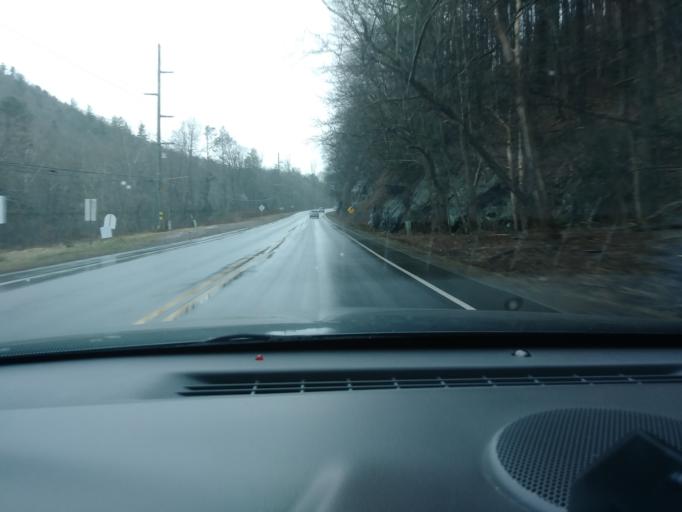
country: US
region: North Carolina
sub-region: Watauga County
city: Foscoe
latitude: 36.1928
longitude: -81.7456
